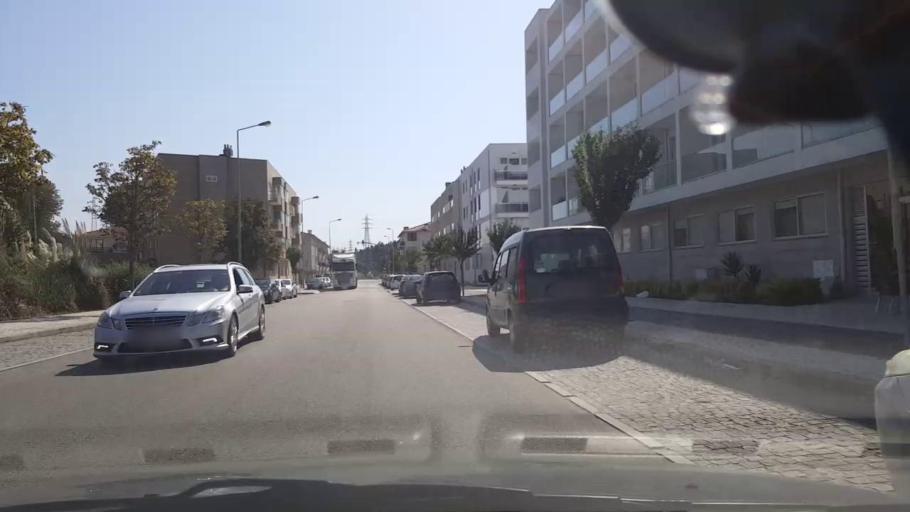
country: PT
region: Porto
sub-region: Vila do Conde
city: Vila do Conde
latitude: 41.3570
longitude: -8.7318
